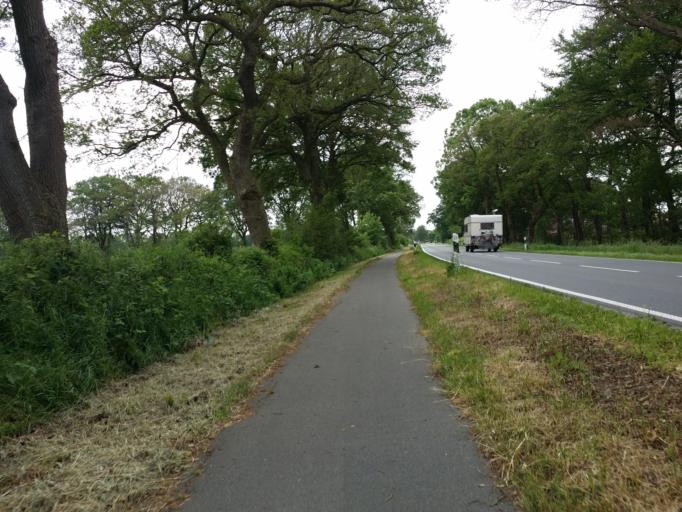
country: DE
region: Lower Saxony
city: Wittmund
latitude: 53.5503
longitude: 7.7836
